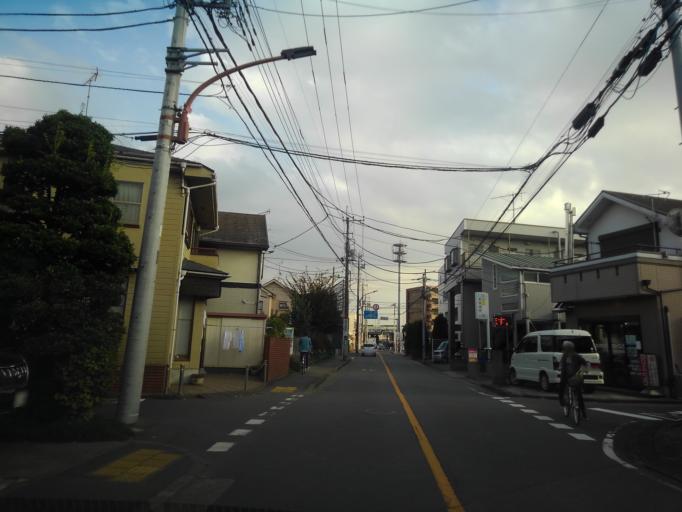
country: JP
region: Tokyo
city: Chofugaoka
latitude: 35.6648
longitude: 139.5415
